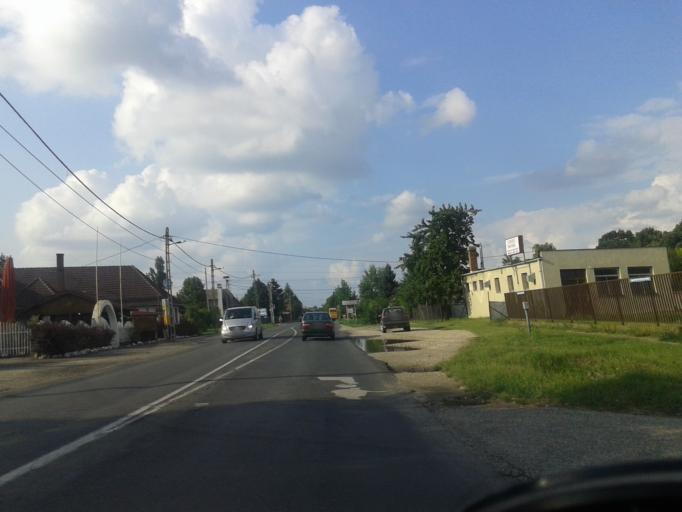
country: HU
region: Pest
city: Kiskunlachaza
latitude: 47.1696
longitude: 19.0002
